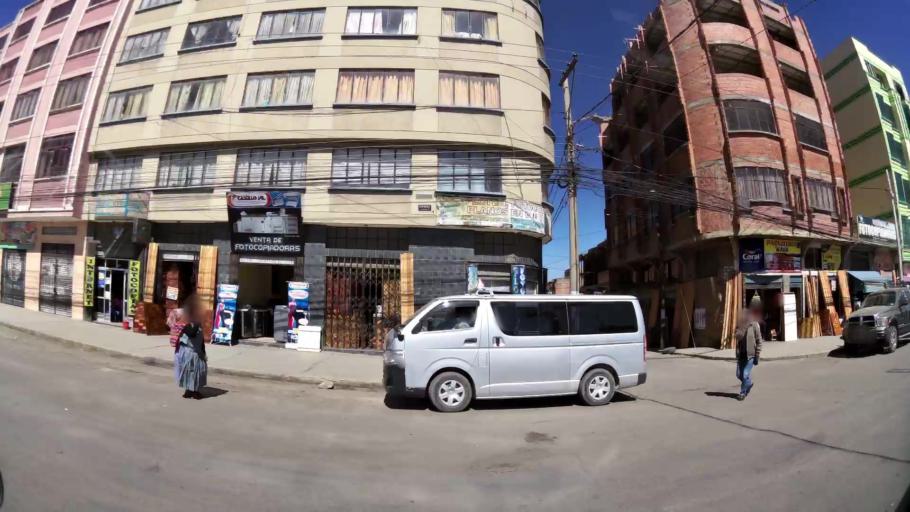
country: BO
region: La Paz
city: La Paz
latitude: -16.5024
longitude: -68.1661
